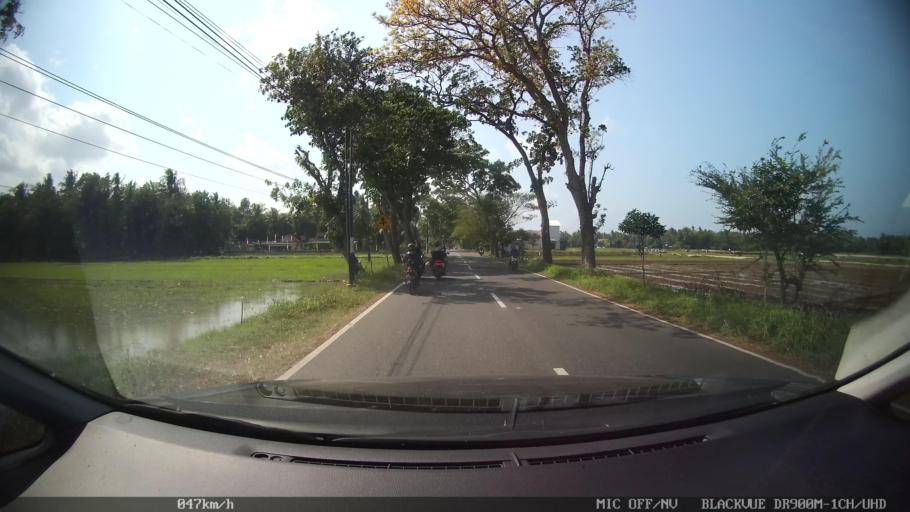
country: ID
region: Daerah Istimewa Yogyakarta
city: Srandakan
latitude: -7.9353
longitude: 110.2203
